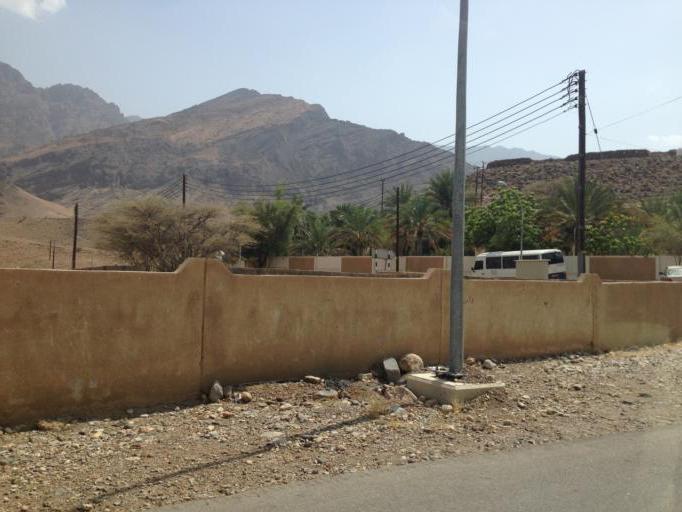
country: OM
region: Ash Sharqiyah
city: Ibra'
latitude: 23.0873
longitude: 58.8645
